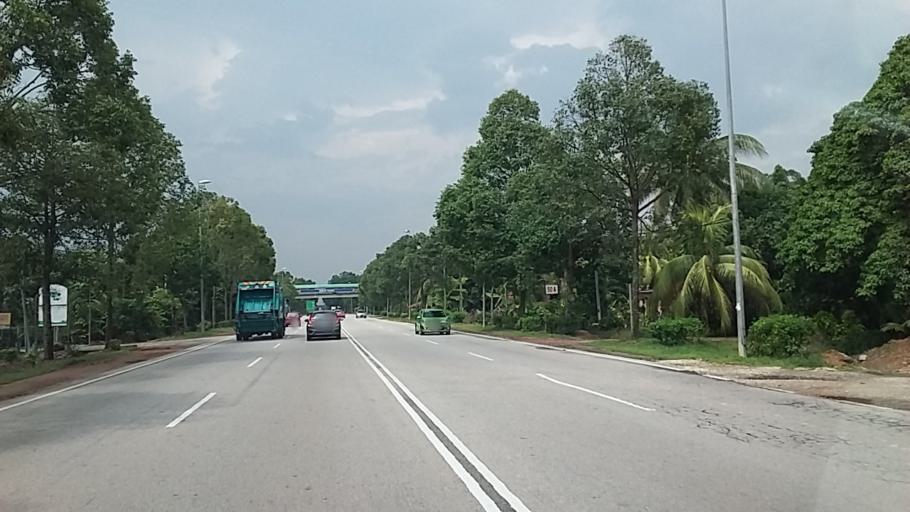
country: MY
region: Johor
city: Parit Raja
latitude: 1.8702
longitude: 103.1268
